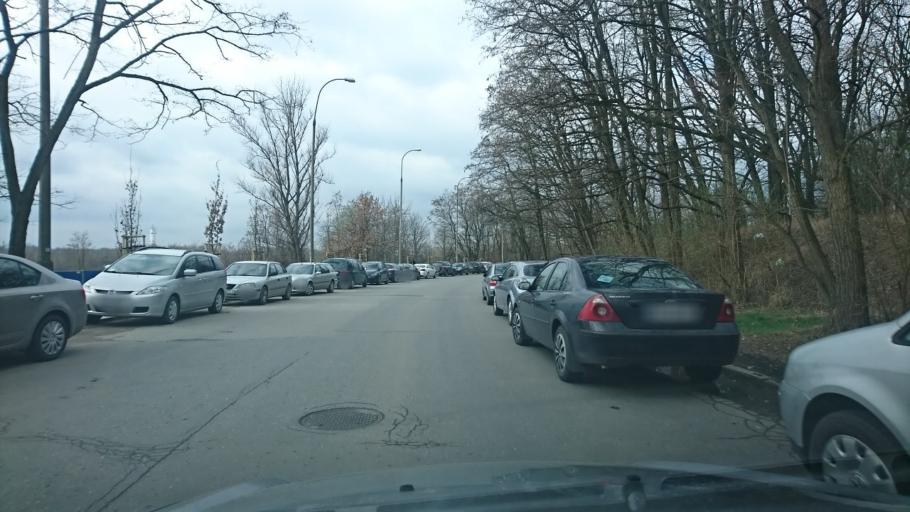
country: PL
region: Lesser Poland Voivodeship
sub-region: Powiat krakowski
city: Ochojno
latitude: 50.0095
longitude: 19.9976
